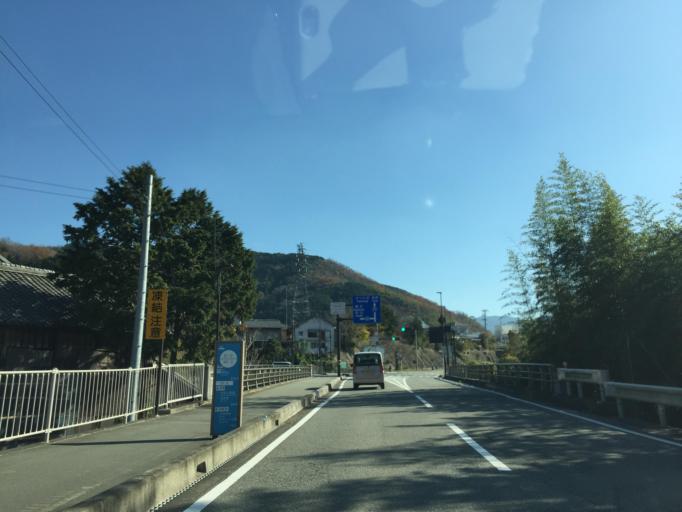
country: JP
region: Wakayama
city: Iwade
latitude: 34.1657
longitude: 135.3041
